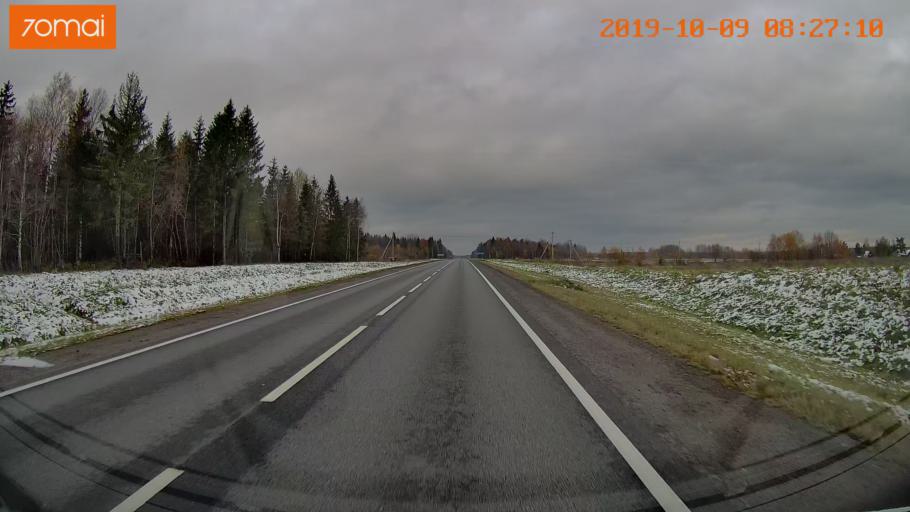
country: RU
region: Vologda
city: Gryazovets
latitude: 58.8004
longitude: 40.2531
